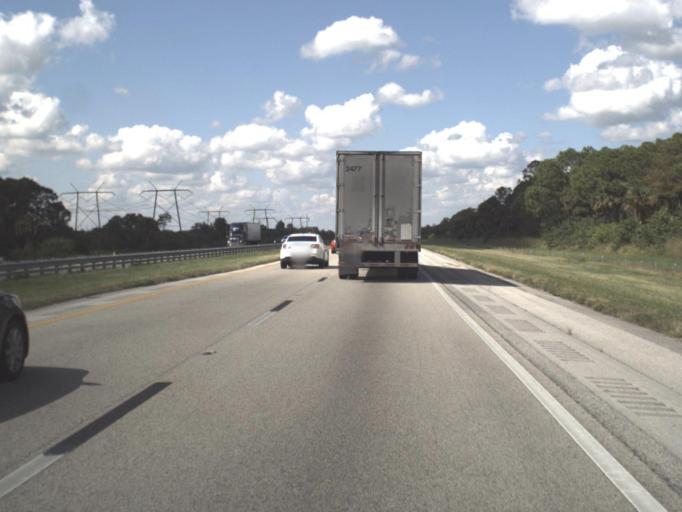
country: US
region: Florida
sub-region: Indian River County
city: West Vero Corridor
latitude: 27.5488
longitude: -80.6309
